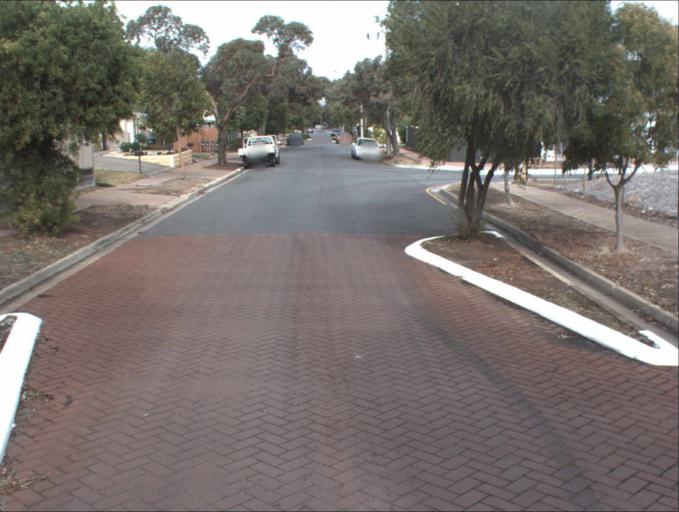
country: AU
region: South Australia
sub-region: Port Adelaide Enfield
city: Gilles Plains
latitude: -34.8482
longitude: 138.6567
